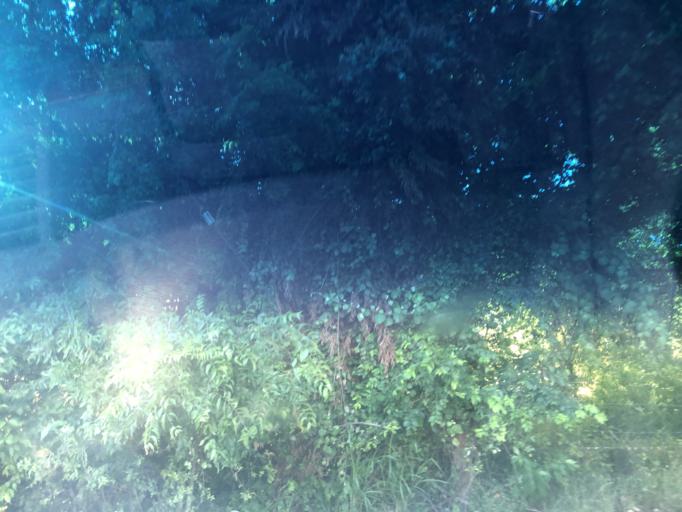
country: US
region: Texas
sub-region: Dallas County
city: Grand Prairie
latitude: 32.7887
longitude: -97.0092
